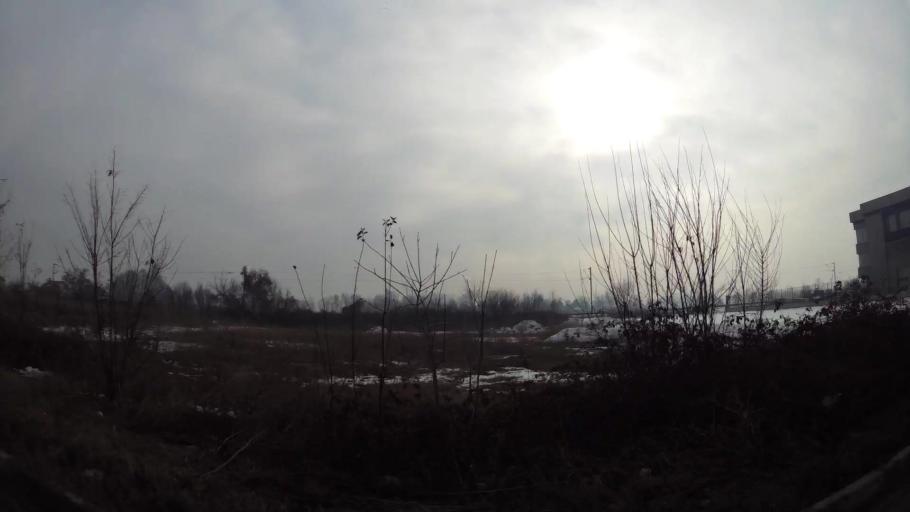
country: MK
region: Ilinden
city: Ilinden
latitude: 41.9949
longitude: 21.5522
